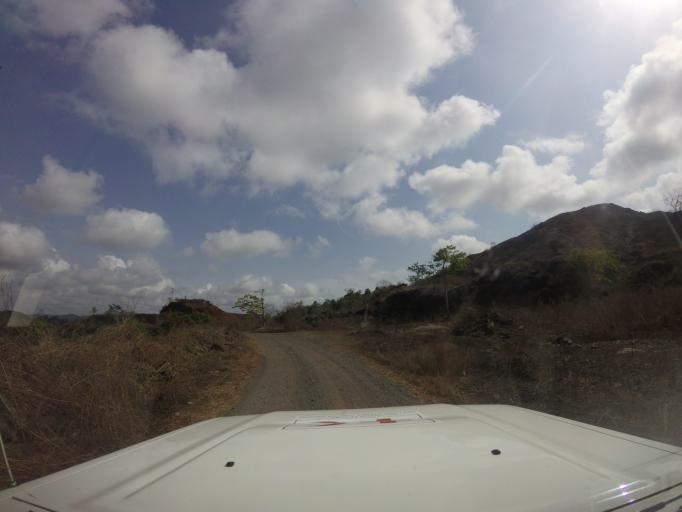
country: LR
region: Bomi
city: Tubmanburg
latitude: 6.8968
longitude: -10.8217
